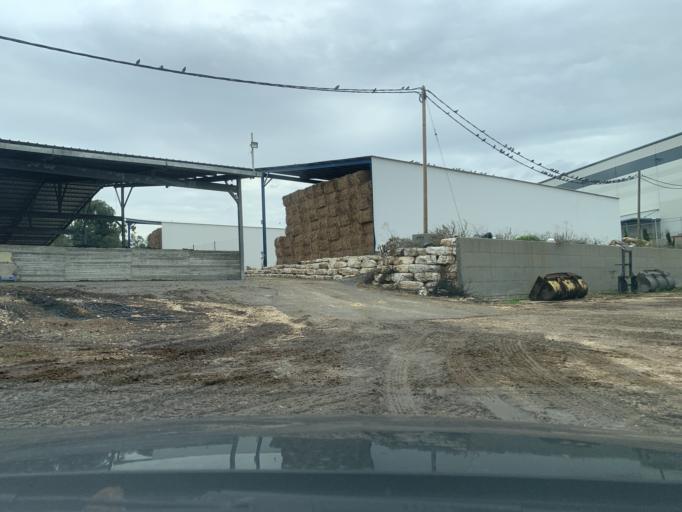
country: PS
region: West Bank
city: Qalqilyah
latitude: 32.2086
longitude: 34.9780
